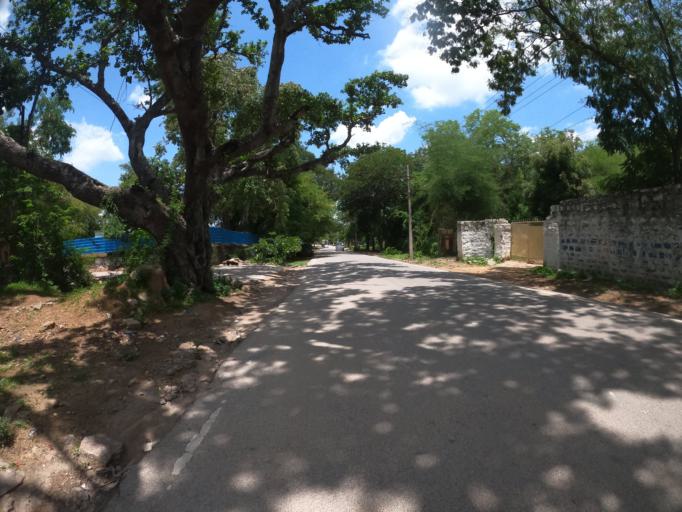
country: IN
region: Telangana
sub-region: Medak
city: Serilingampalle
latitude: 17.3862
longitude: 78.3184
